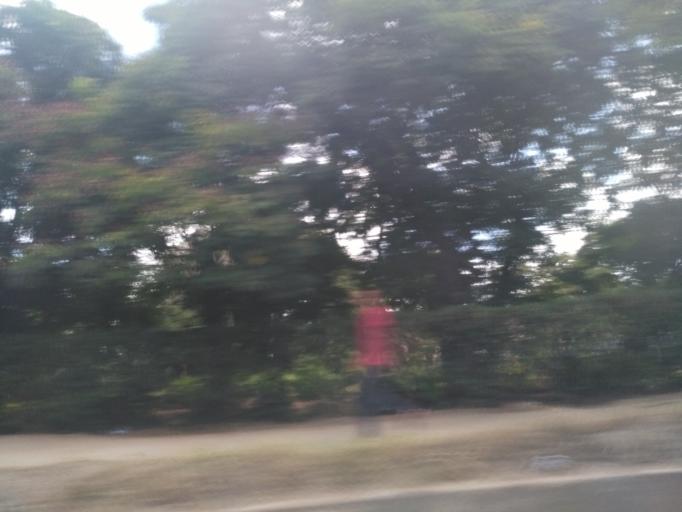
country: TZ
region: Dar es Salaam
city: Dar es Salaam
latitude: -6.8672
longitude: 39.2735
